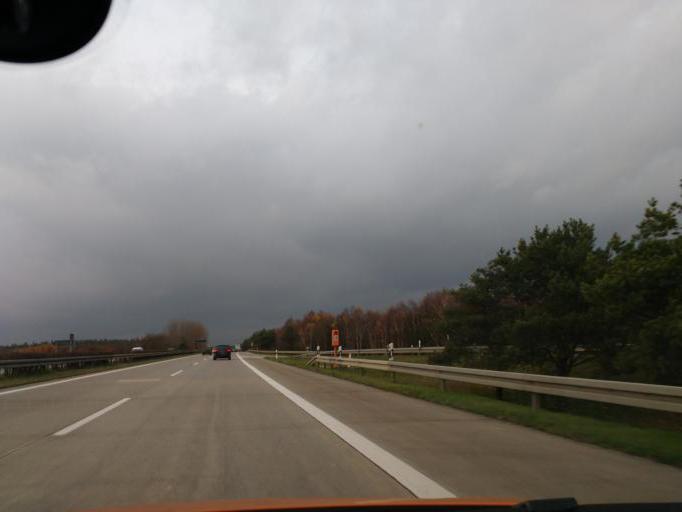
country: DE
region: Brandenburg
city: Heiligengrabe
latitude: 53.1505
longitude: 12.4045
